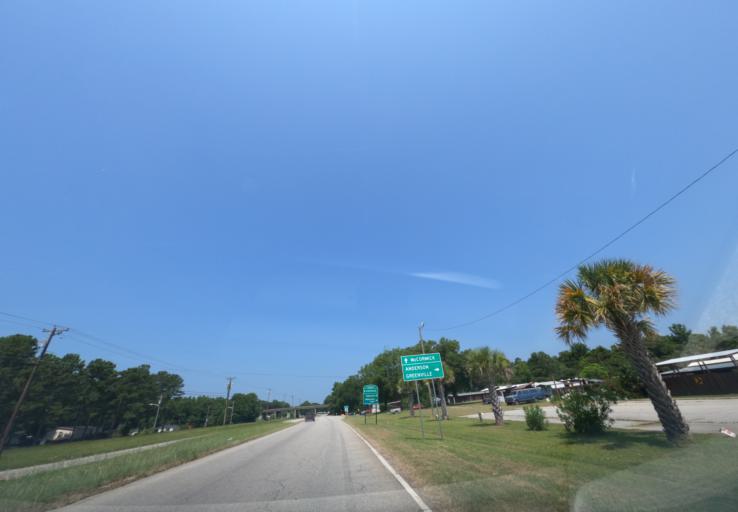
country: US
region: South Carolina
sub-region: Greenwood County
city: Greenwood
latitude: 34.1644
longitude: -82.1228
